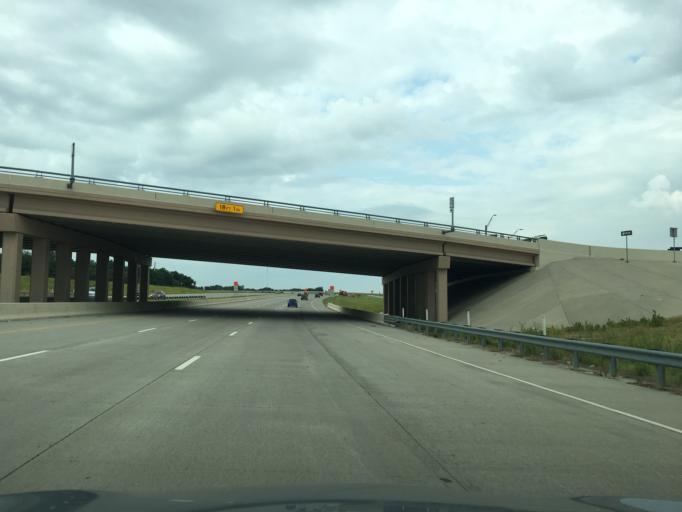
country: US
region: Texas
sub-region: Collin County
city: Melissa
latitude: 33.2705
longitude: -96.5945
